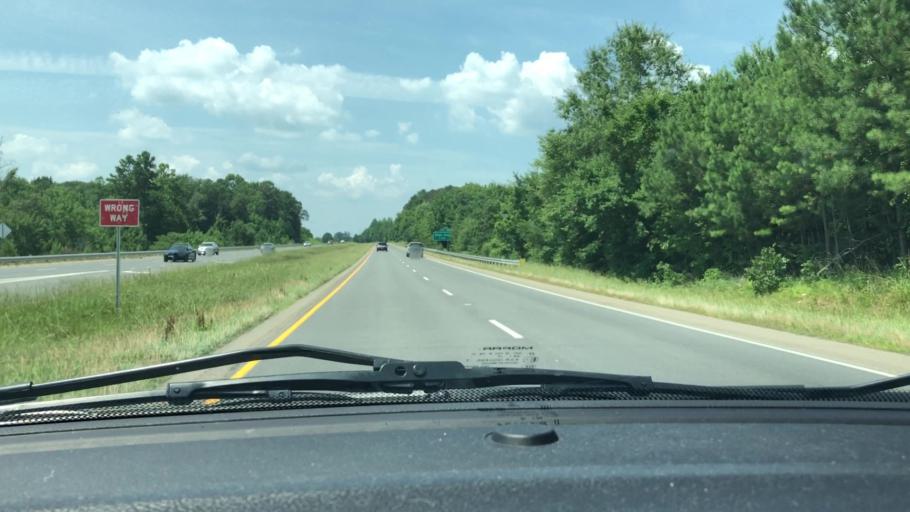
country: US
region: North Carolina
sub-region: Chatham County
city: Siler City
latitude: 35.6776
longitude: -79.4145
